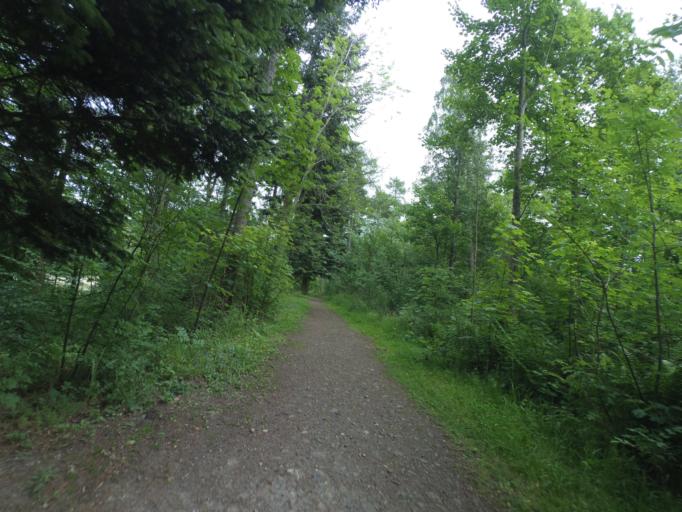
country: GB
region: Scotland
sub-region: East Lothian
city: Pencaitland
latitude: 55.9142
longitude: -2.9036
